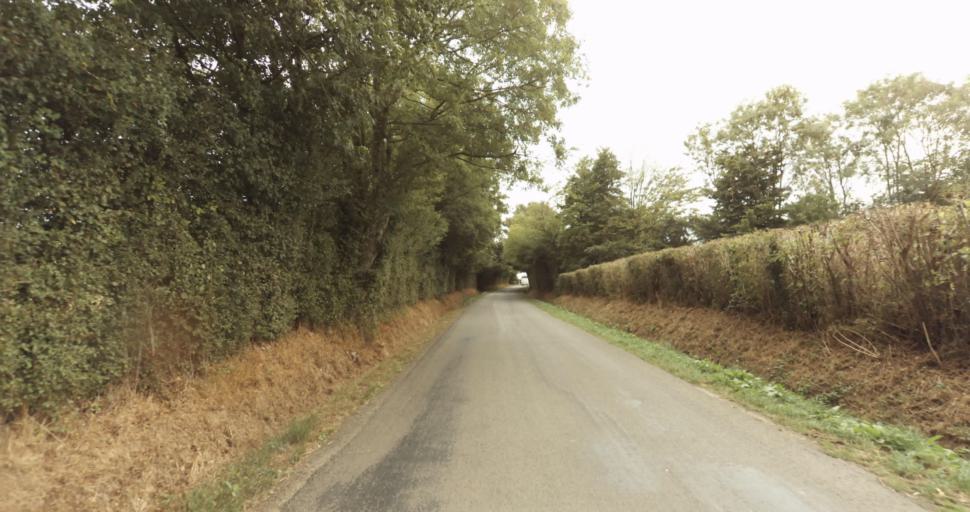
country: FR
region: Lower Normandy
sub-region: Departement de l'Orne
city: Gace
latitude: 48.8831
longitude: 0.3453
